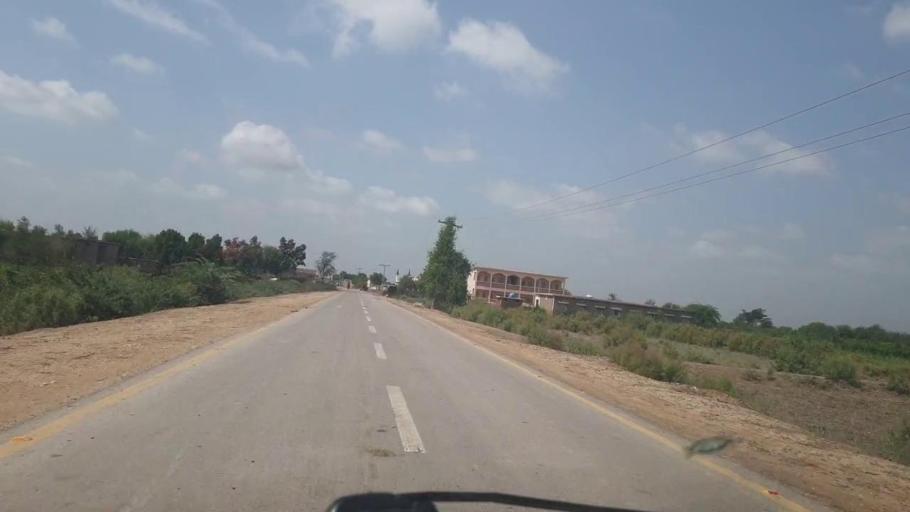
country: PK
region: Sindh
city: Berani
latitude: 25.6795
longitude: 68.9251
